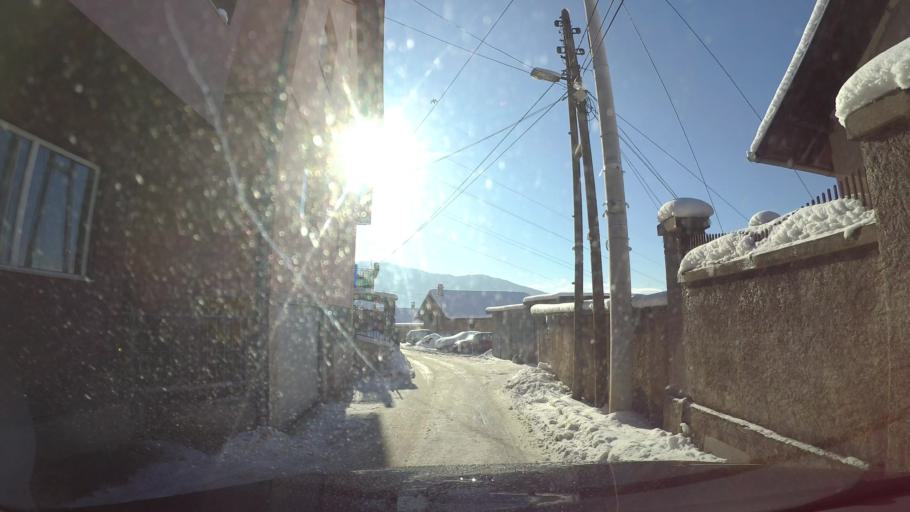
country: BA
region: Federation of Bosnia and Herzegovina
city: Kobilja Glava
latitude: 43.8749
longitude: 18.4224
